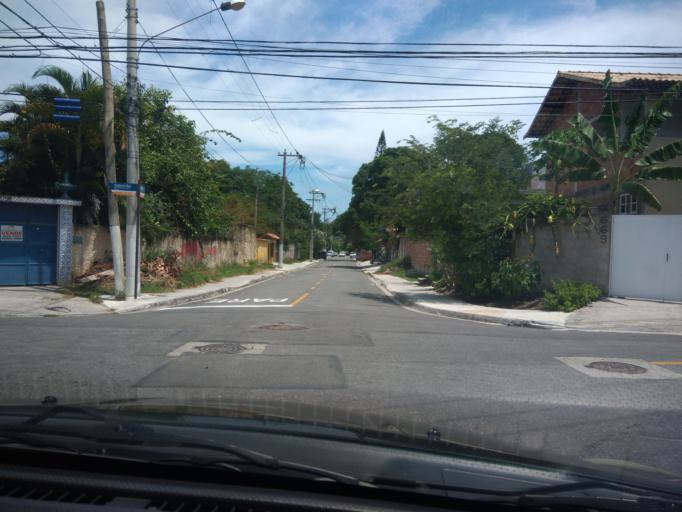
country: BR
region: Rio de Janeiro
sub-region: Niteroi
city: Niteroi
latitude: -22.9308
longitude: -43.0728
